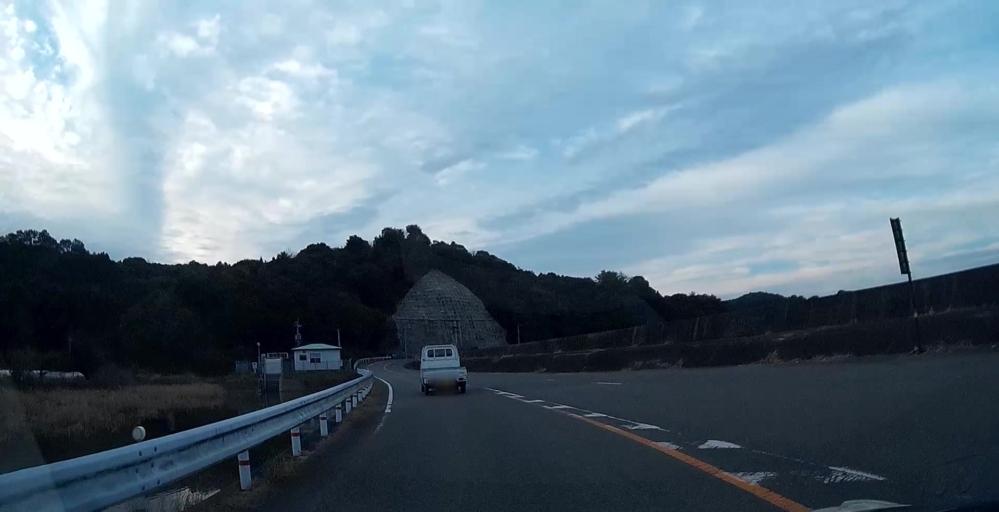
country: JP
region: Kumamoto
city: Hondo
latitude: 32.5002
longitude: 130.3924
